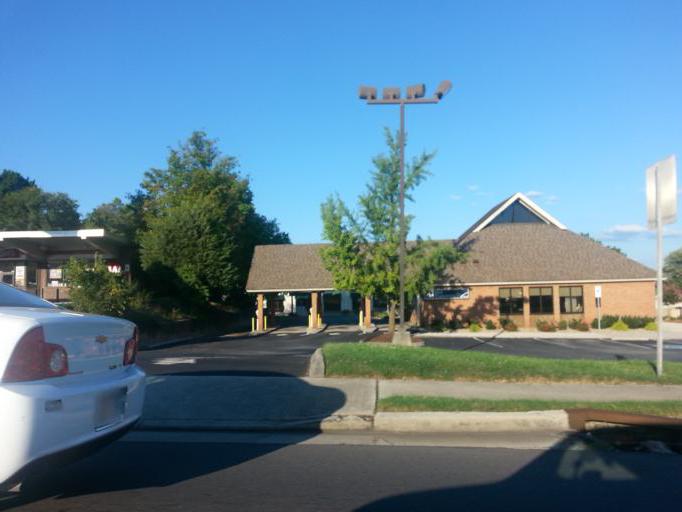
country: US
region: Tennessee
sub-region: Knox County
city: Farragut
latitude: 35.9215
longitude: -84.0926
